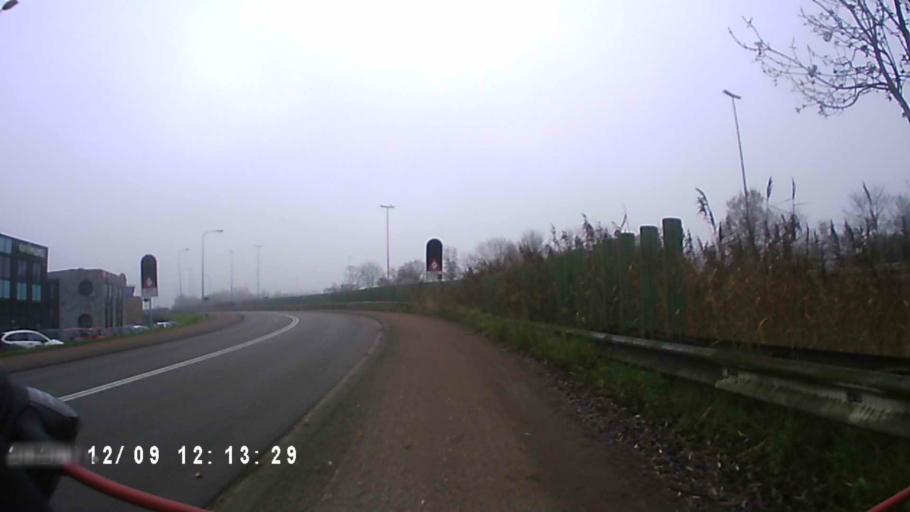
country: NL
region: Groningen
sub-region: Gemeente Groningen
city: Oosterpark
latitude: 53.2026
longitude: 6.6066
